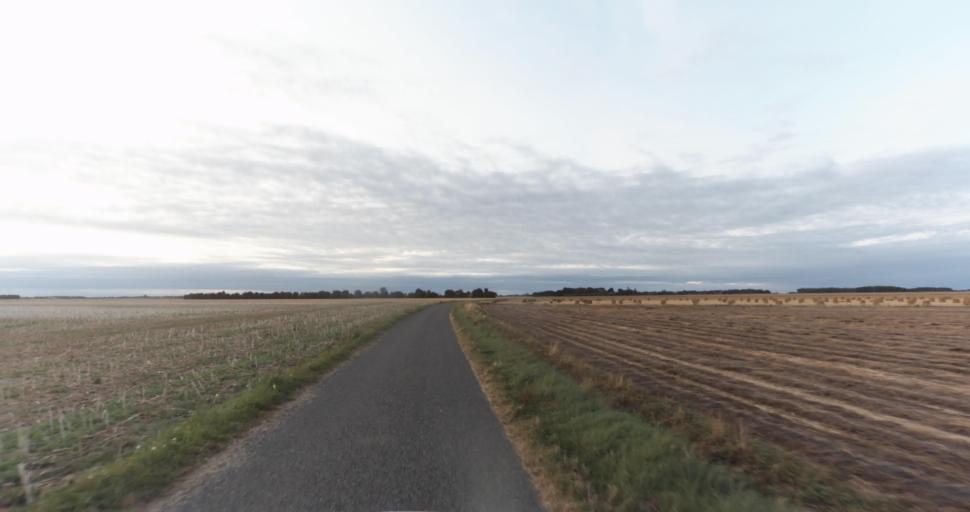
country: FR
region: Haute-Normandie
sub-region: Departement de l'Eure
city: La Madeleine-de-Nonancourt
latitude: 48.8692
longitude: 1.2303
